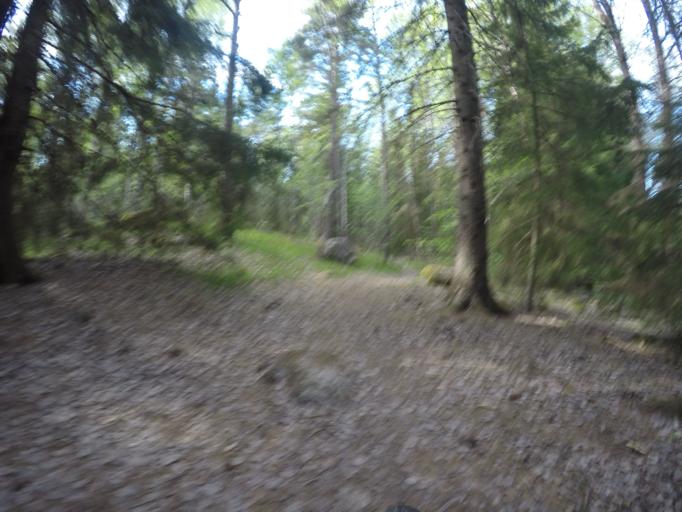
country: SE
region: Vaestmanland
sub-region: Vasteras
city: Vasteras
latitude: 59.6566
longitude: 16.5108
